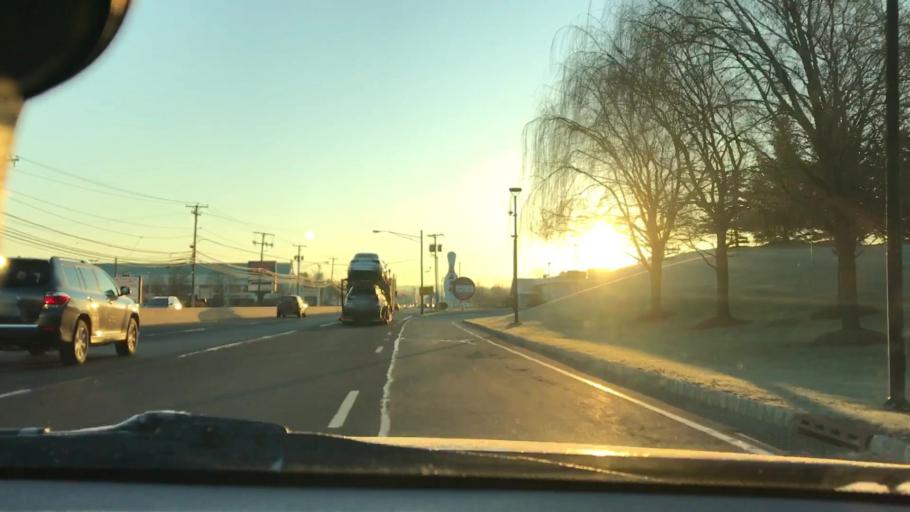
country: US
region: New Jersey
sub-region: Morris County
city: Hanover
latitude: 40.8107
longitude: -74.3847
